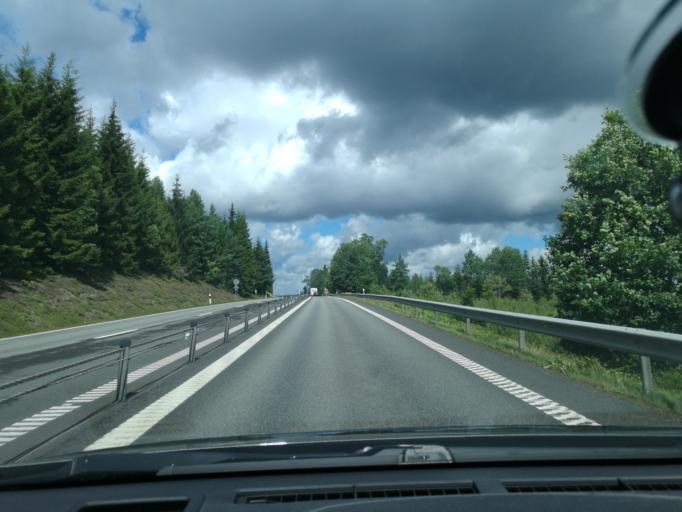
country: SE
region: Skane
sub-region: Osby Kommun
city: Osby
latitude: 56.3805
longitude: 14.0370
